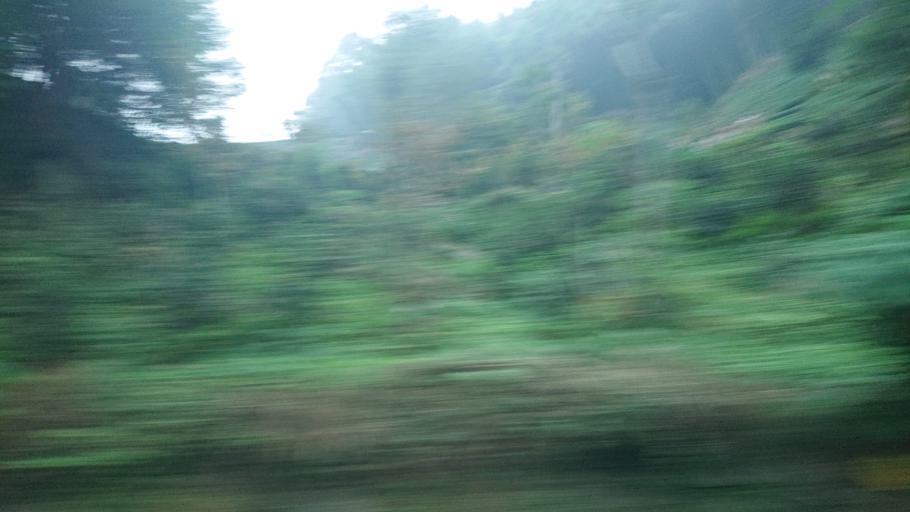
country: TW
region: Taiwan
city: Lugu
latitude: 23.5263
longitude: 120.7082
